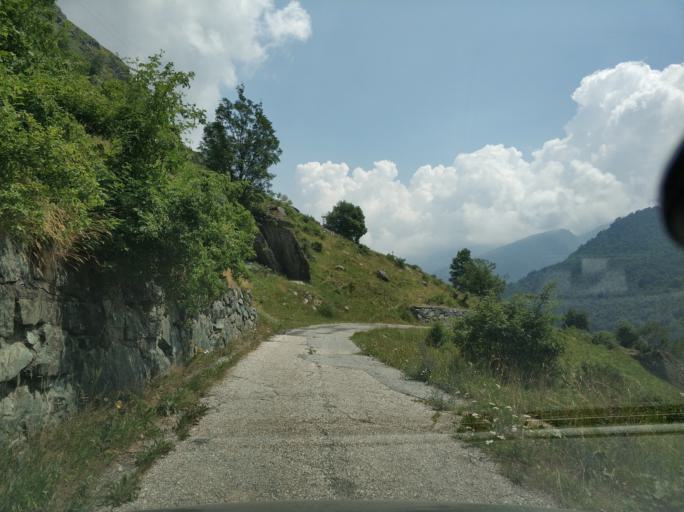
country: IT
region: Piedmont
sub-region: Provincia di Torino
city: Usseglio
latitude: 45.2452
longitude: 7.1826
